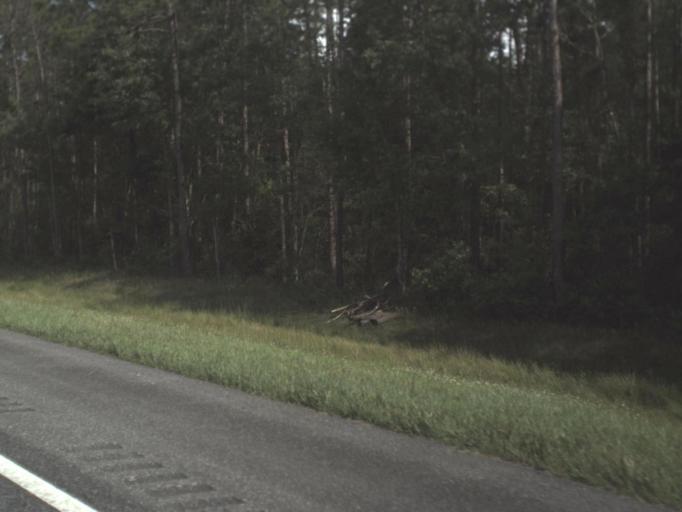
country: US
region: Florida
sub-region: Union County
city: Lake Butler
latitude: 30.2541
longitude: -82.3533
